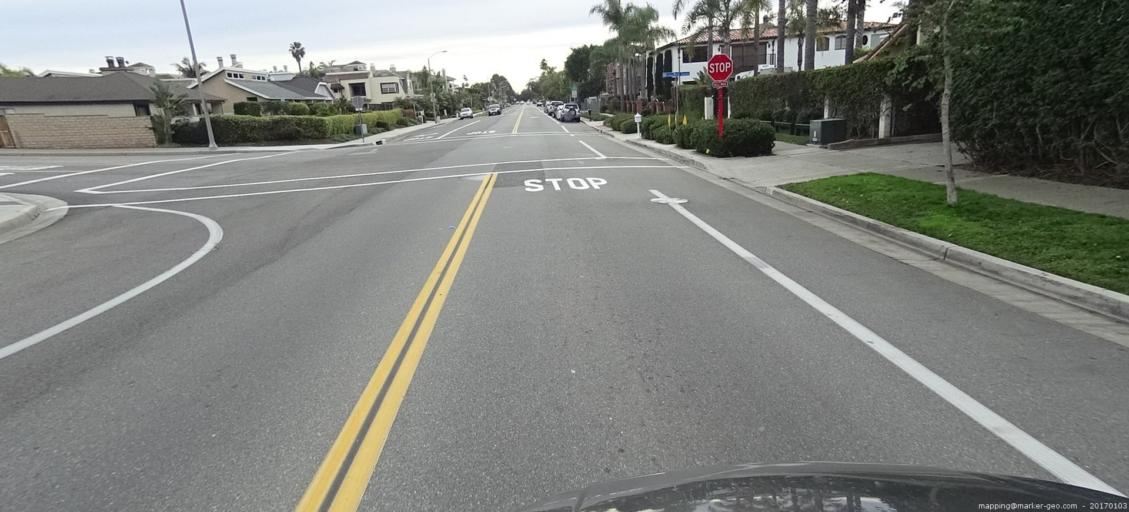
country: US
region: California
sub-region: Orange County
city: Dana Point
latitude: 33.4494
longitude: -117.6542
